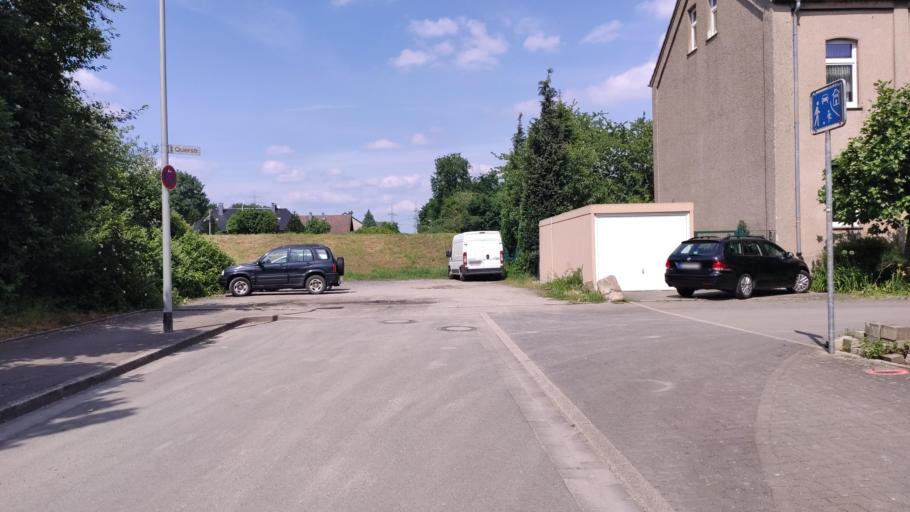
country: DE
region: North Rhine-Westphalia
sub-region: Regierungsbezirk Munster
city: Gelsenkirchen
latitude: 51.5448
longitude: 7.1361
